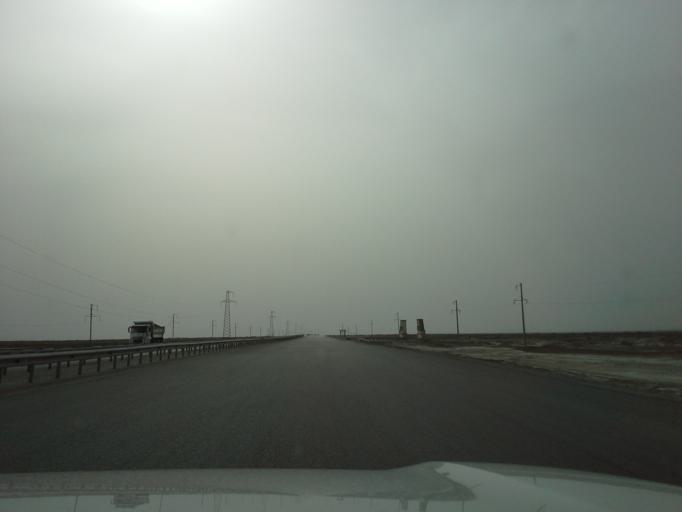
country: TM
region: Ahal
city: Kaka
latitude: 37.5290
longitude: 59.4170
